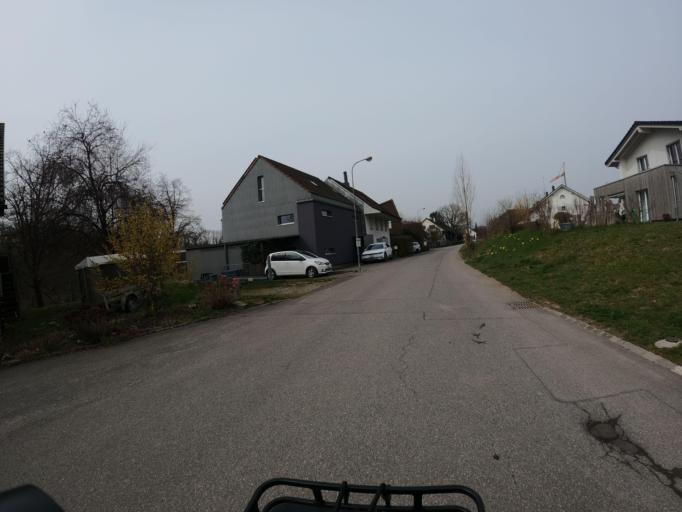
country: CH
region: Aargau
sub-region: Bezirk Lenzburg
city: Niederlenz
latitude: 47.4114
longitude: 8.1863
